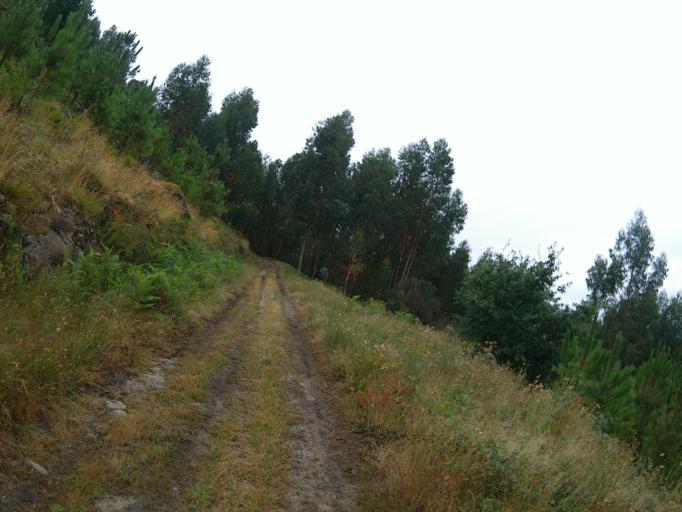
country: PT
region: Viana do Castelo
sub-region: Ponte de Lima
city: Ponte de Lima
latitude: 41.7265
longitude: -8.6078
